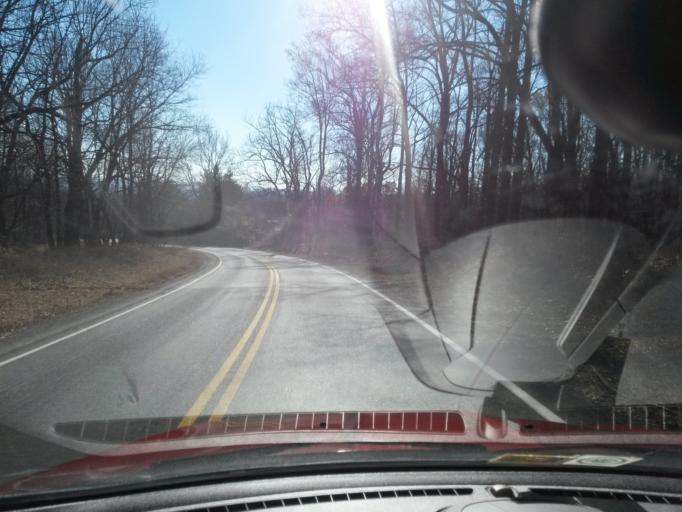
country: US
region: Virginia
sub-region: City of Bedford
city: Bedford
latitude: 37.4310
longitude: -79.5754
